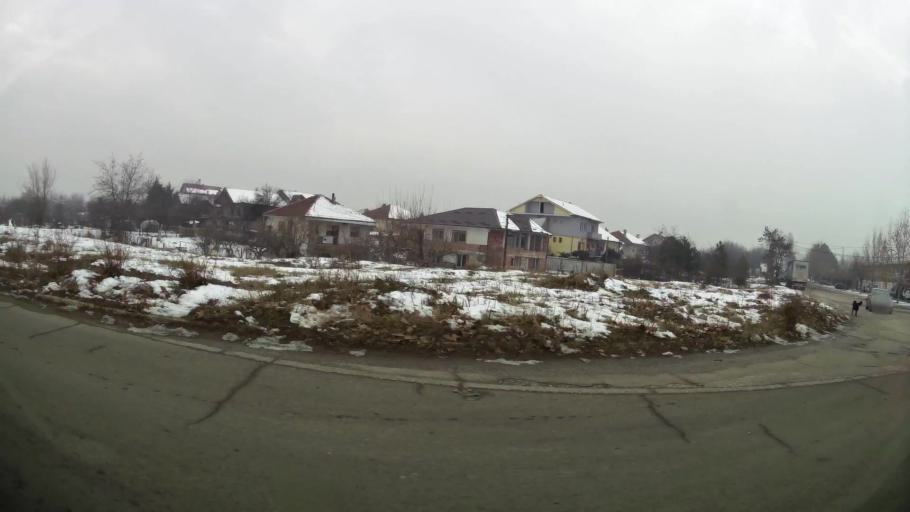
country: MK
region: Saraj
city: Saraj
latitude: 42.0176
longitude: 21.3626
